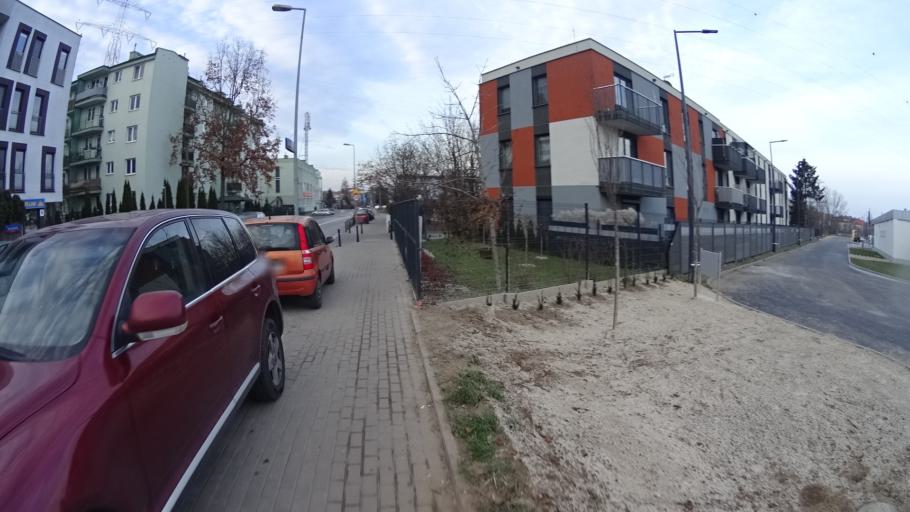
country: PL
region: Masovian Voivodeship
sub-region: Warszawa
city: Bielany
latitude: 52.3233
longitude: 20.9387
